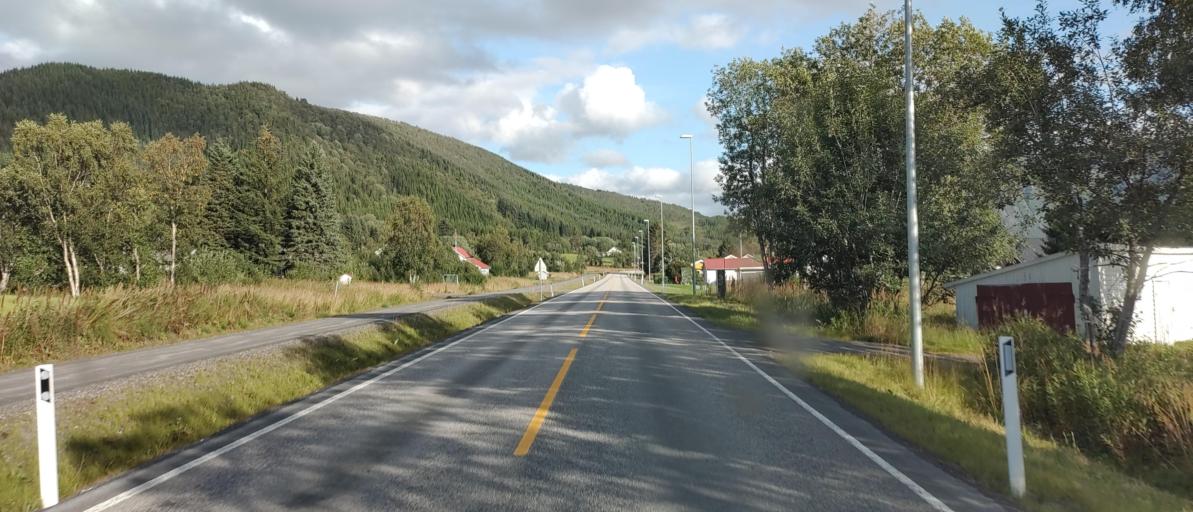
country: NO
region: Nordland
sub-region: Sortland
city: Sortland
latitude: 68.7513
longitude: 15.4821
